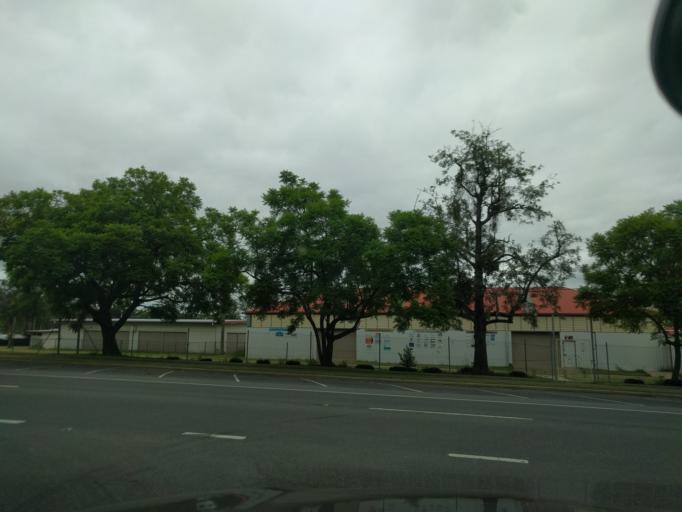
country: AU
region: Queensland
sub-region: Logan
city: Cedar Vale
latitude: -27.9916
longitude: 153.0034
